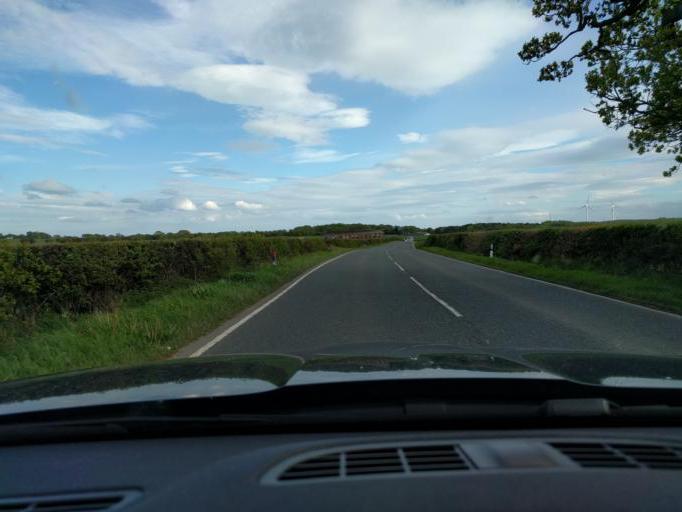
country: GB
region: England
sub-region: Northumberland
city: Choppington
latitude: 55.1239
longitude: -1.6318
